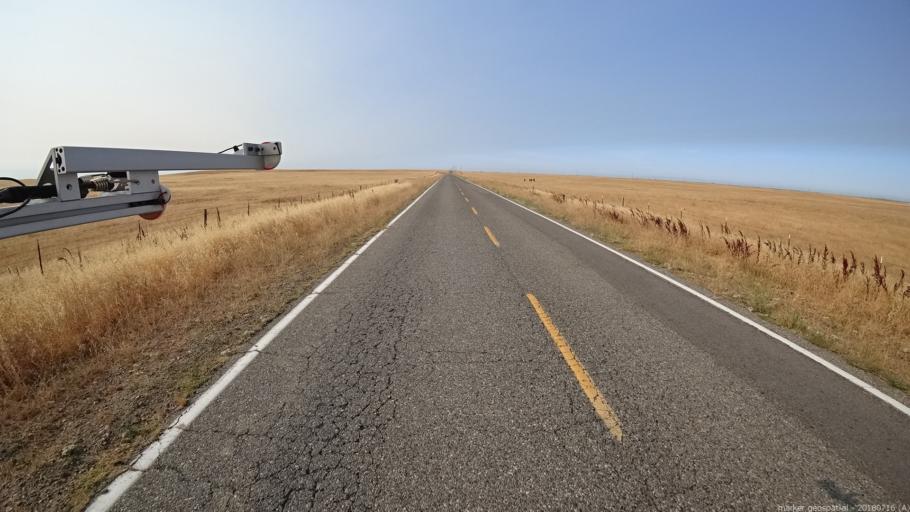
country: US
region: California
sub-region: Madera County
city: Madera Acres
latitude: 37.1337
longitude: -120.0203
